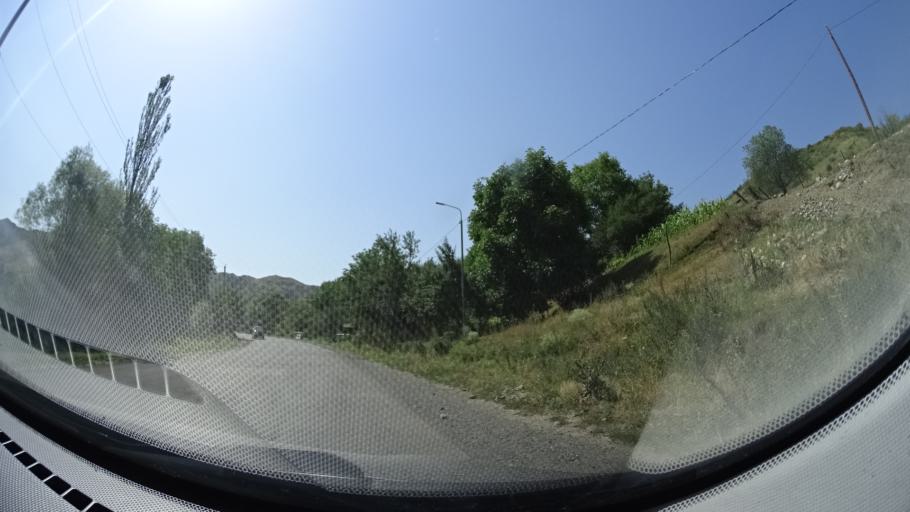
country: GE
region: Samtskhe-Javakheti
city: Akhaltsikhe
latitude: 41.6320
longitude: 43.0443
